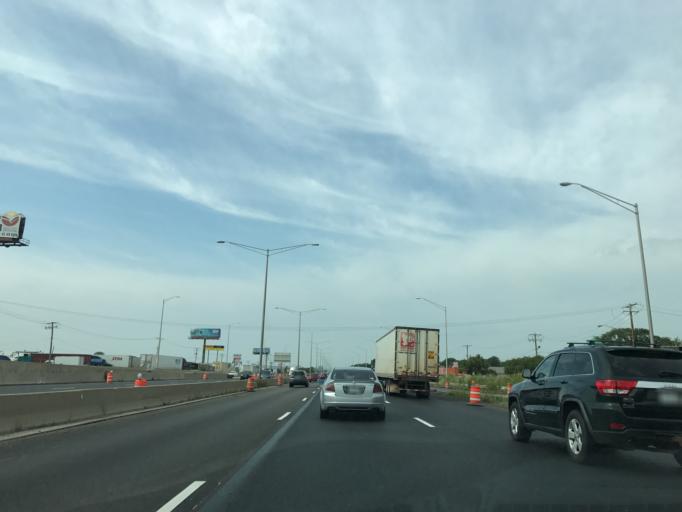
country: US
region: Illinois
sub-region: Will County
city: Bolingbrook
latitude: 41.6987
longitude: -88.0419
